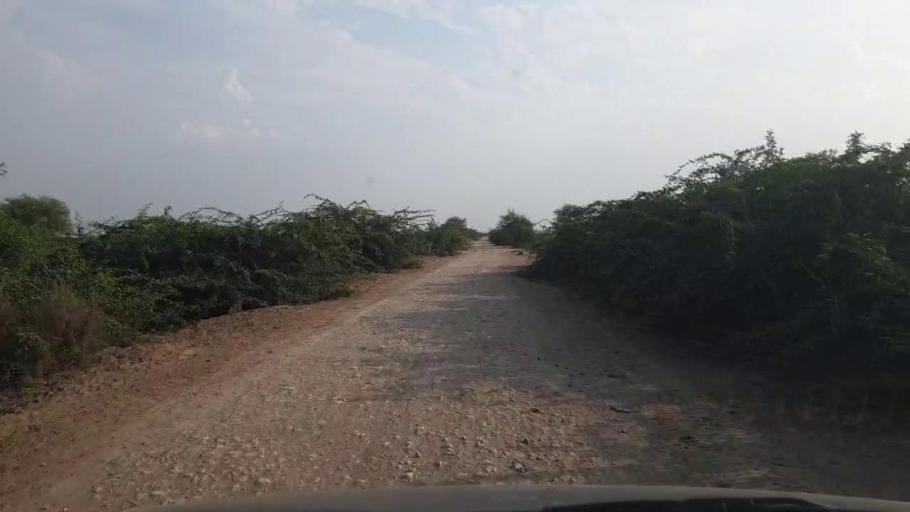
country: PK
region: Sindh
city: Badin
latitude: 24.5654
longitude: 68.6675
